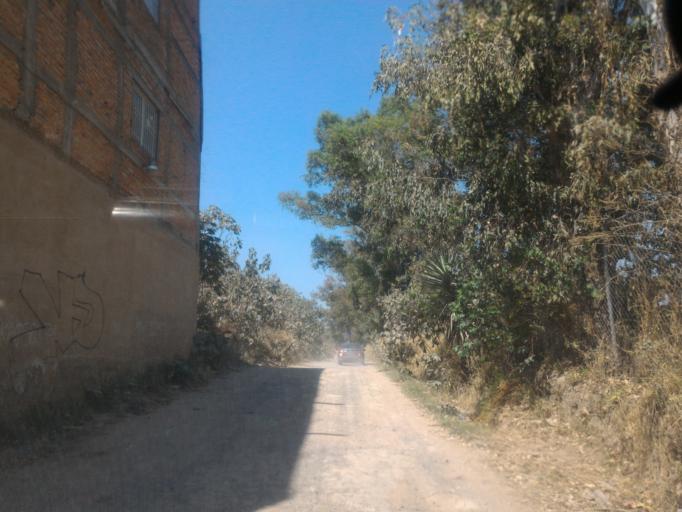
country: MX
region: Jalisco
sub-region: San Pedro Tlaquepaque
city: Paseo del Prado
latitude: 20.5627
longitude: -103.4033
